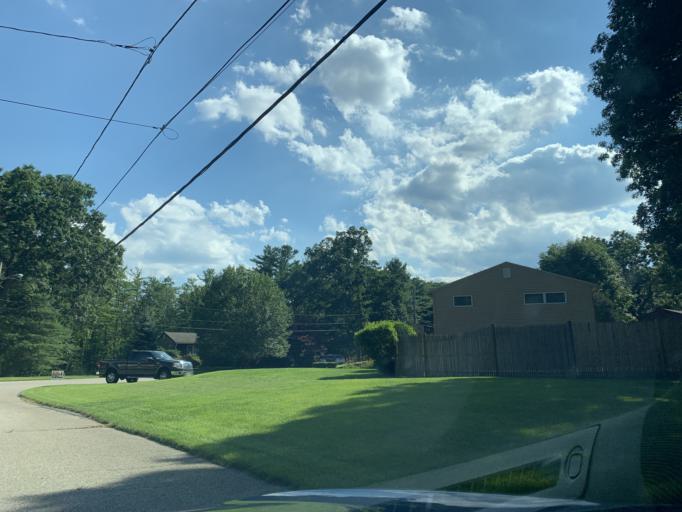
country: US
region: Rhode Island
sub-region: Kent County
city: East Greenwich
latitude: 41.6193
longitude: -71.4463
